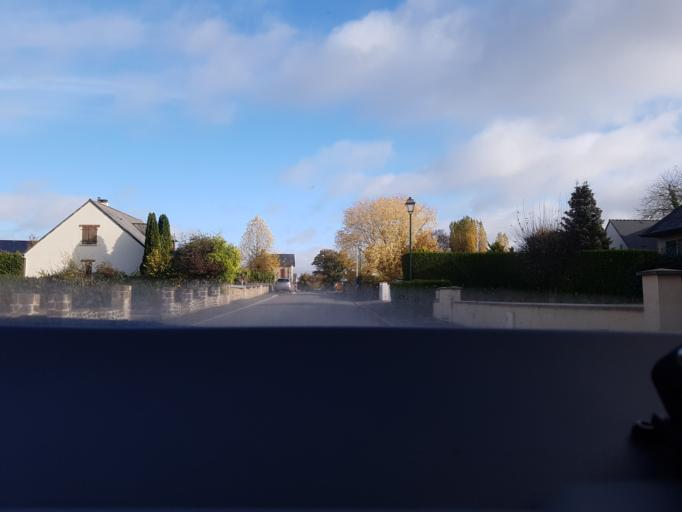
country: FR
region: Pays de la Loire
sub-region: Departement de la Mayenne
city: Ambrieres-les-Vallees
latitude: 48.3859
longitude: -0.5849
